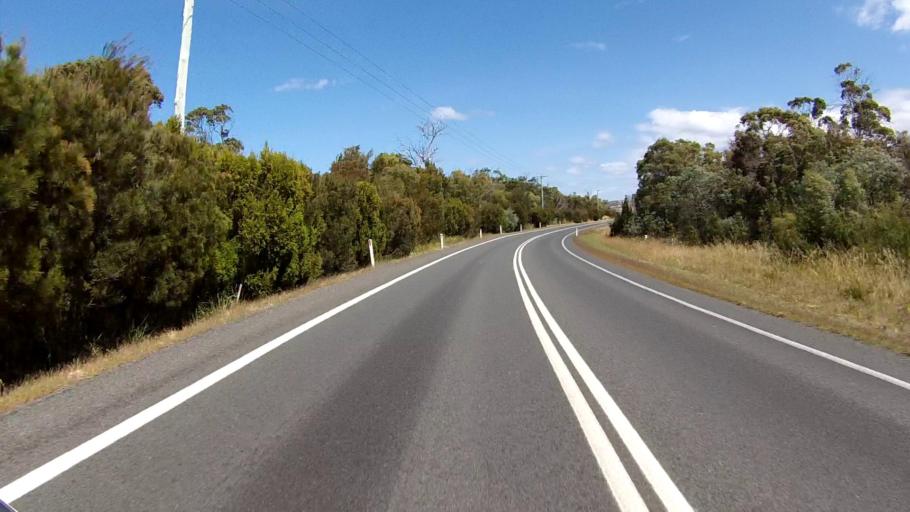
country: AU
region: Tasmania
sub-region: Break O'Day
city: St Helens
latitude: -42.0820
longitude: 148.0687
